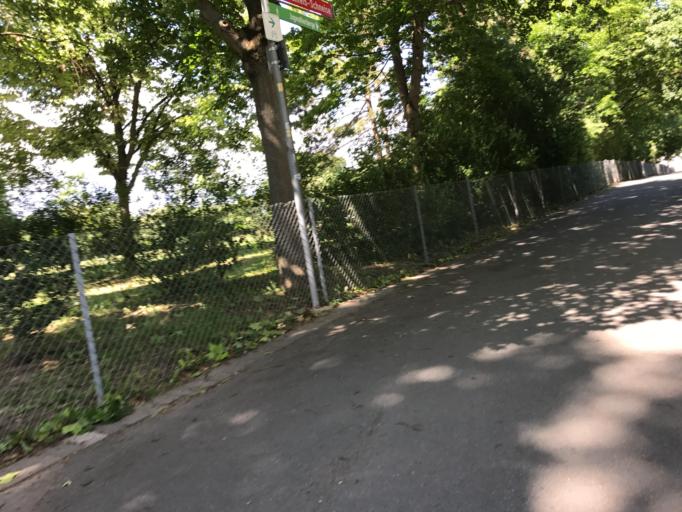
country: DE
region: Rheinland-Pfalz
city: Mainz
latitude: 49.9855
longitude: 8.2935
